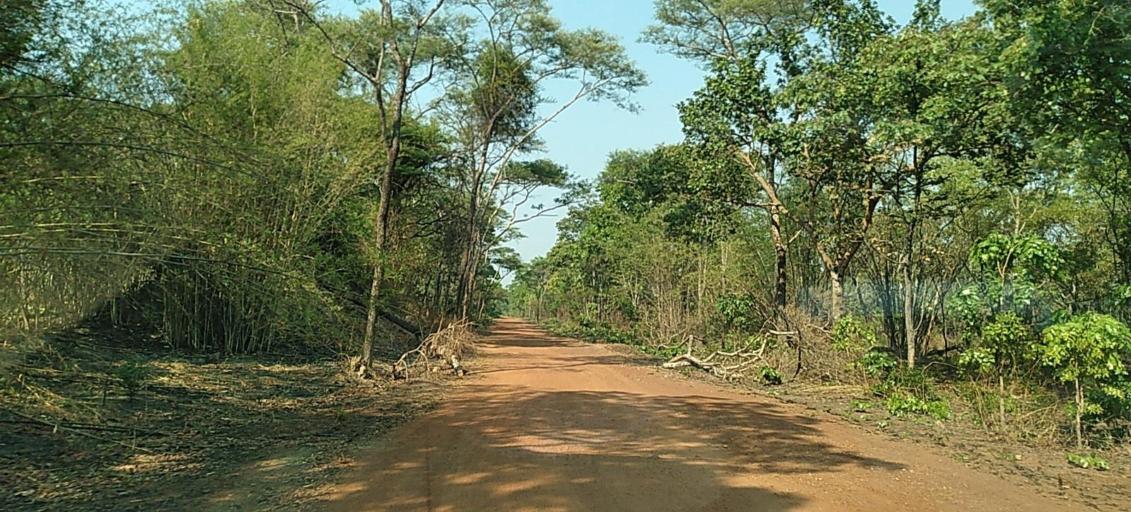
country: ZM
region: Copperbelt
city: Chingola
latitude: -12.8707
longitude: 27.4531
